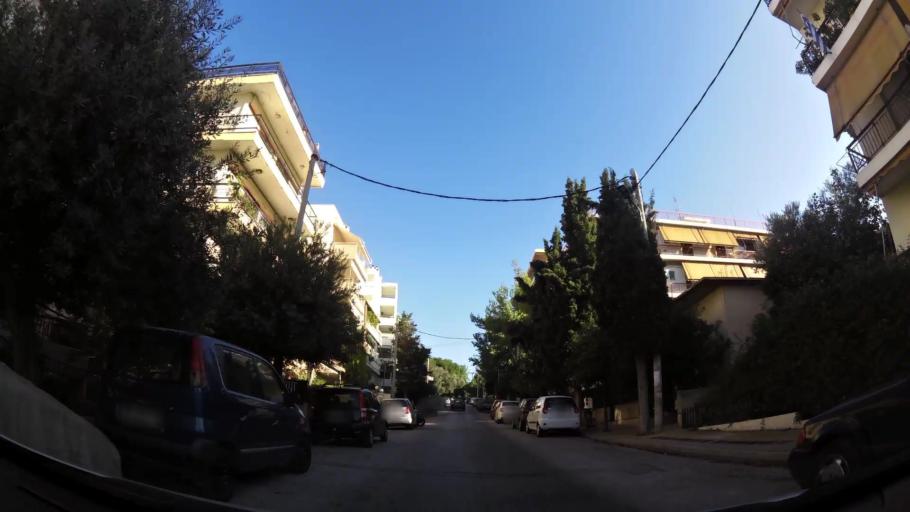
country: GR
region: Attica
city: Pefki
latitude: 38.0506
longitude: 23.7900
